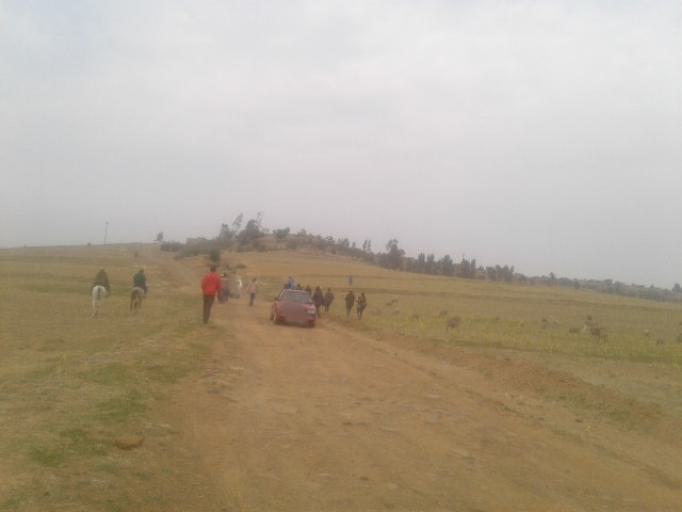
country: LS
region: Berea
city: Teyateyaneng
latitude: -29.0838
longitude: 27.9044
